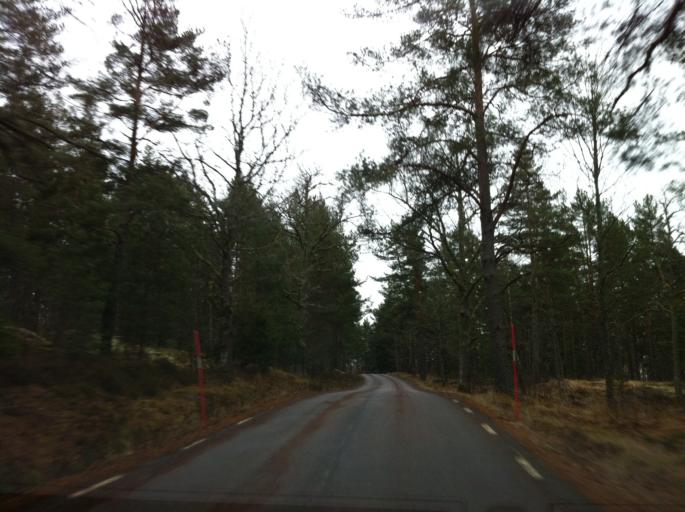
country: SE
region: Kalmar
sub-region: Vasterviks Kommun
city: Forserum
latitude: 57.9282
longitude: 16.5298
